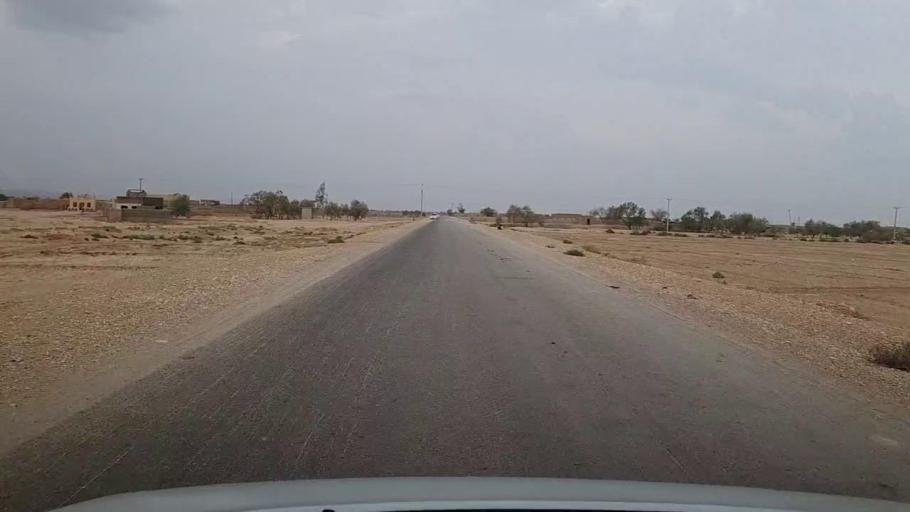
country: PK
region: Sindh
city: Sehwan
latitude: 26.3358
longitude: 67.7180
